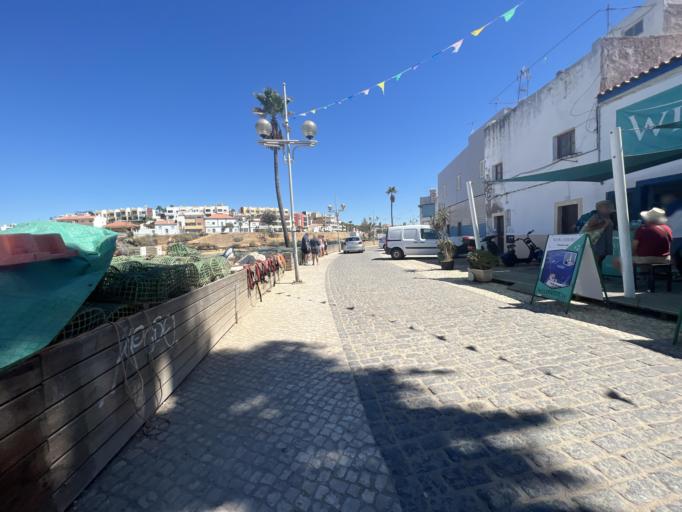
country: PT
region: Faro
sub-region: Portimao
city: Portimao
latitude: 37.1245
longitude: -8.5222
